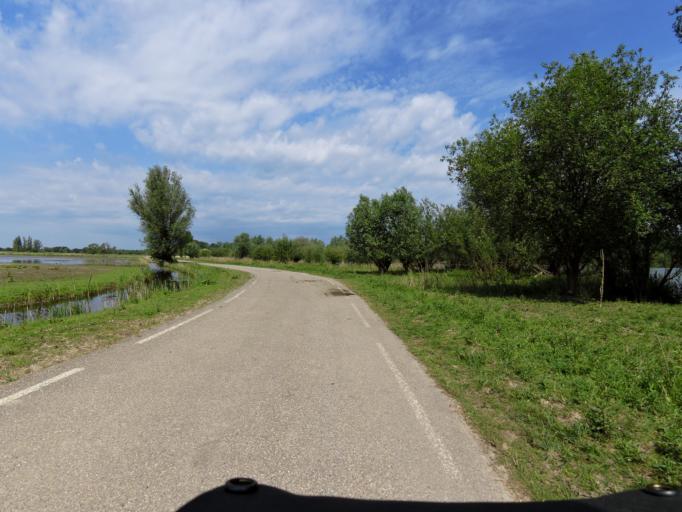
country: NL
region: North Brabant
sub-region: Gemeente Woudrichem
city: Woudrichem
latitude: 51.8116
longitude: 5.0314
